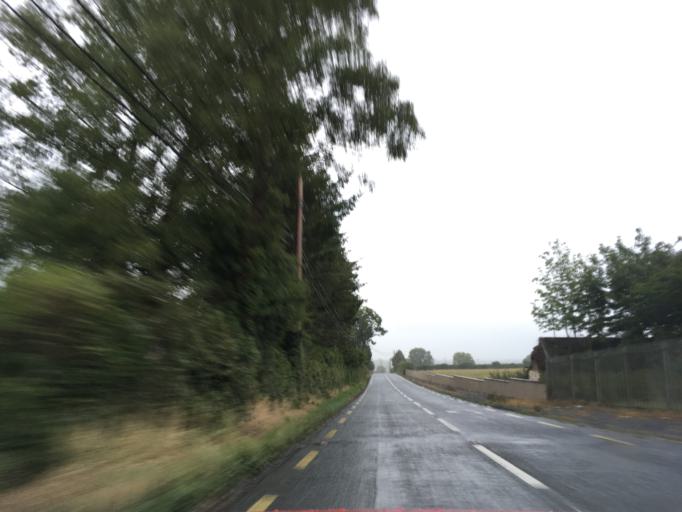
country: IE
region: Munster
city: Tipperary
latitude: 52.4829
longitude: -8.0837
